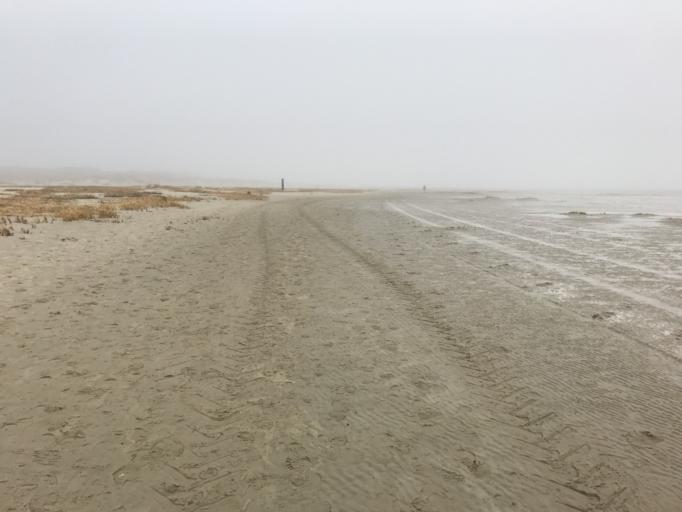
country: DE
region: Lower Saxony
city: Borkum
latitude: 53.6049
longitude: 6.6878
